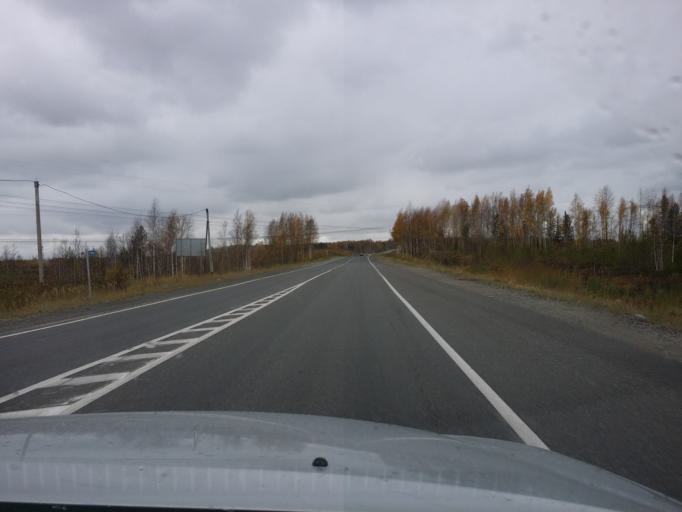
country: RU
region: Khanty-Mansiyskiy Avtonomnyy Okrug
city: Megion
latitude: 61.1085
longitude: 76.0126
